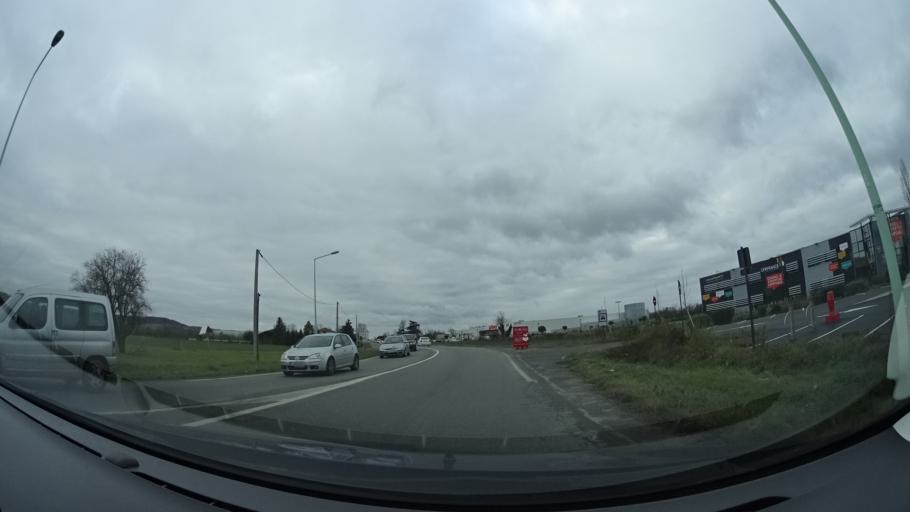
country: FR
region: Aquitaine
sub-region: Departement du Lot-et-Garonne
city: Bias
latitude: 44.4031
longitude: 0.6699
